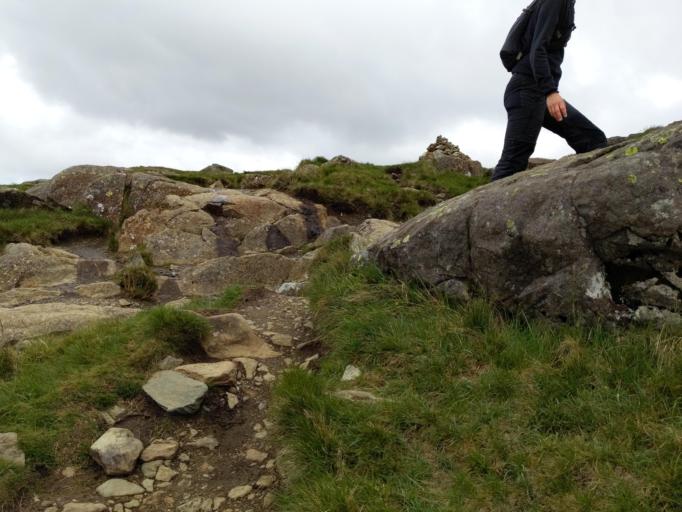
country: GB
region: Wales
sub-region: Gwynedd
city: Llanberis
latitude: 53.0579
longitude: -4.1014
